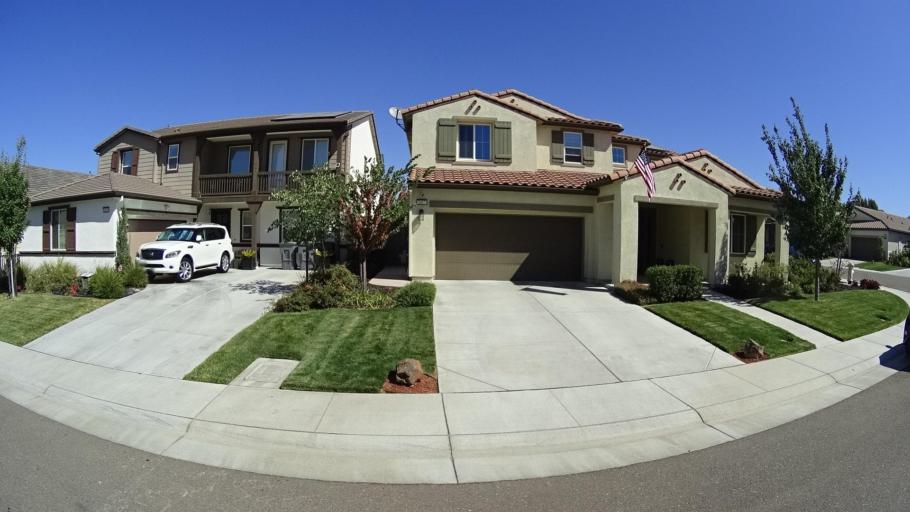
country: US
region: California
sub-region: Placer County
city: Lincoln
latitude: 38.8297
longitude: -121.2853
